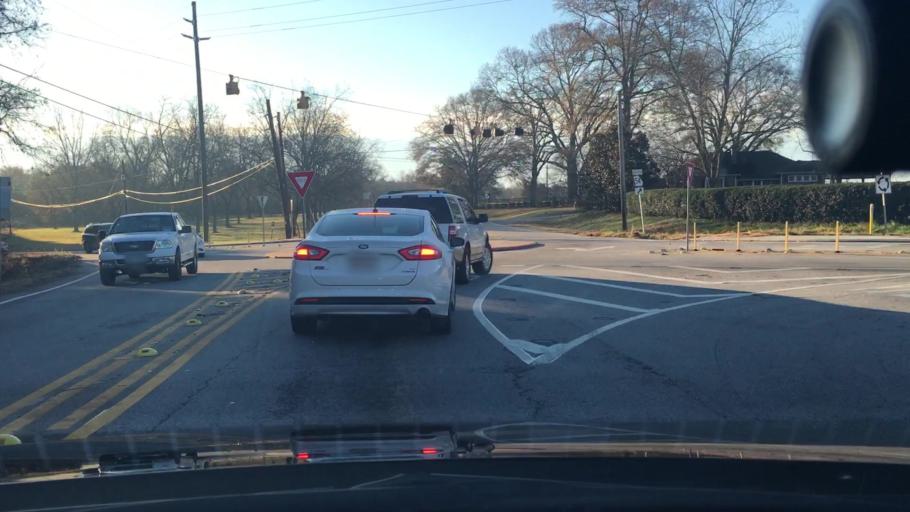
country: US
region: Georgia
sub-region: Fayette County
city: Peachtree City
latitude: 33.3301
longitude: -84.6450
